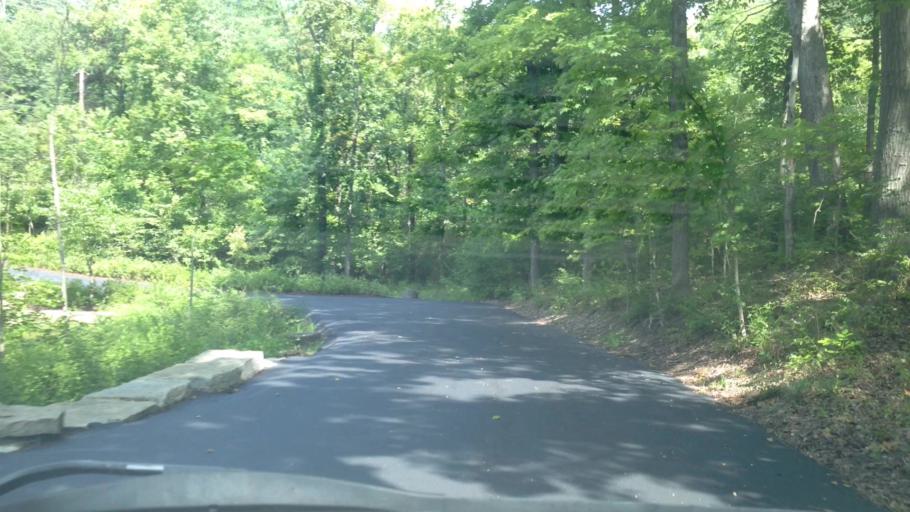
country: US
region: Missouri
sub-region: Saint Louis County
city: Des Peres
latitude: 38.5825
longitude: -90.4431
